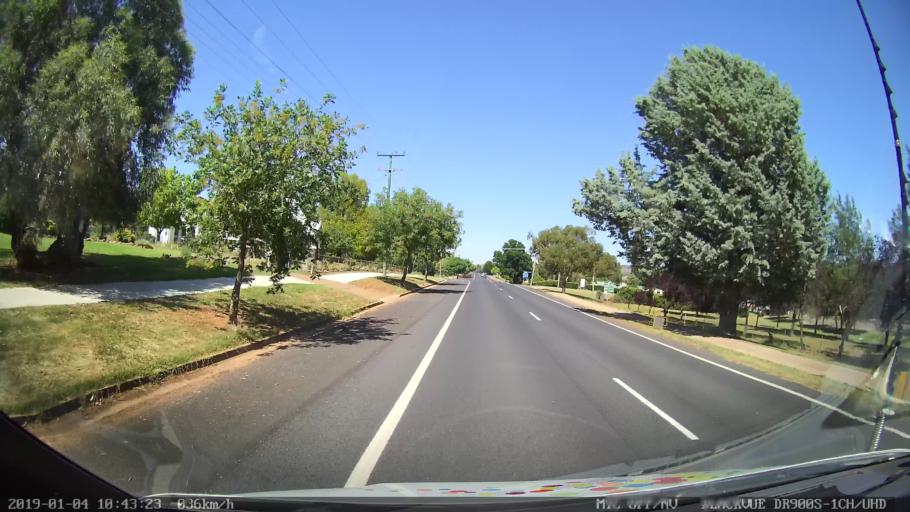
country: AU
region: New South Wales
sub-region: Cabonne
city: Molong
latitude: -33.2846
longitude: 148.7442
